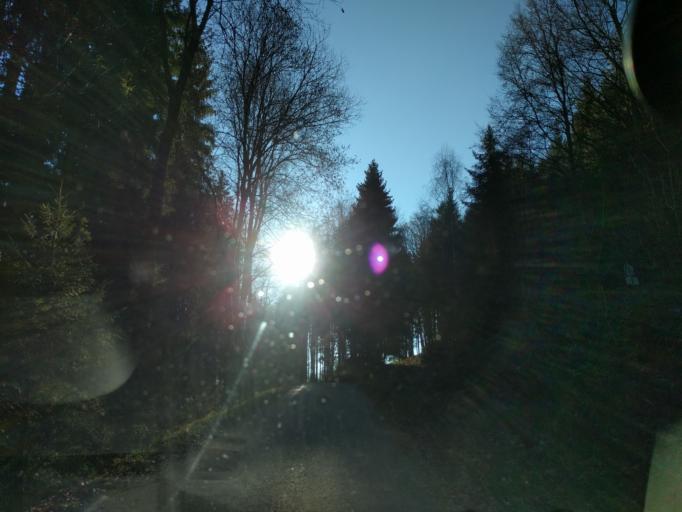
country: AT
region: Upper Austria
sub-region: Politischer Bezirk Urfahr-Umgebung
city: Kirchschlag bei Linz
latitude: 48.4136
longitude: 14.2882
